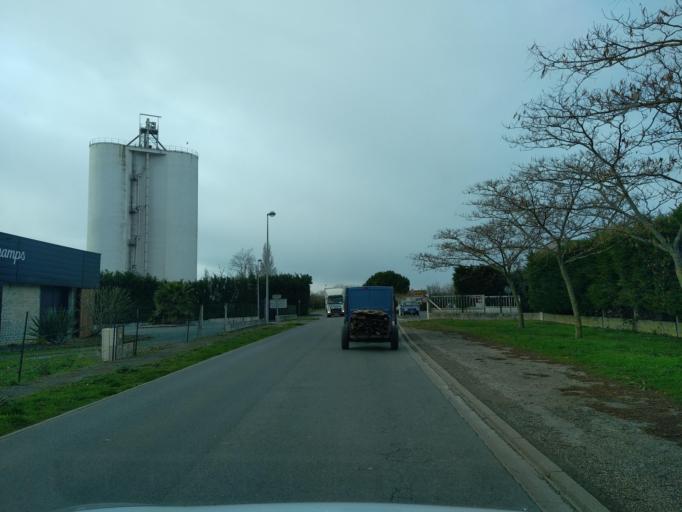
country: FR
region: Pays de la Loire
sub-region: Departement de la Vendee
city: Vix
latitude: 46.3686
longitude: -0.8699
